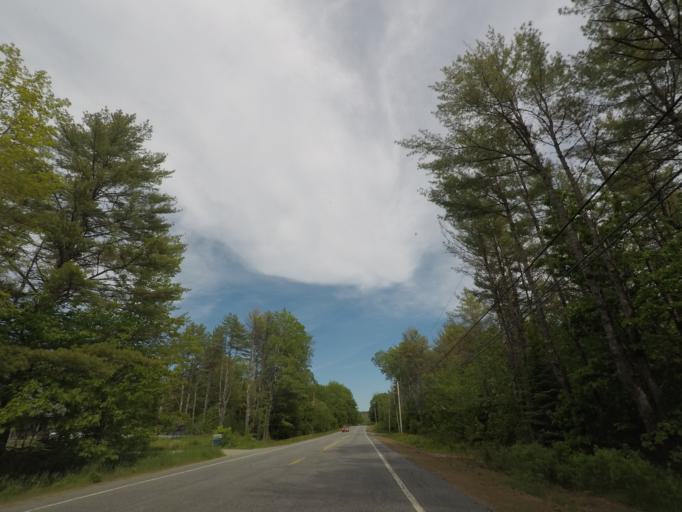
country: US
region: Maine
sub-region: Sagadahoc County
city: Richmond
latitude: 44.0864
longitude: -69.7632
